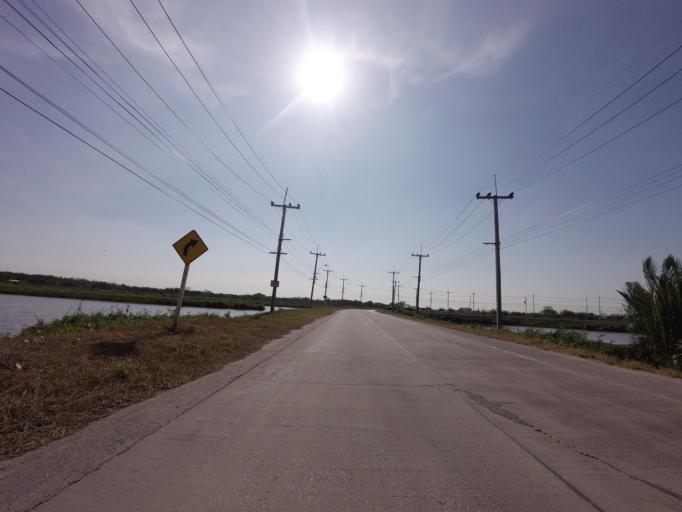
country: TH
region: Samut Prakan
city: Phra Samut Chedi
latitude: 13.5535
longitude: 100.5364
